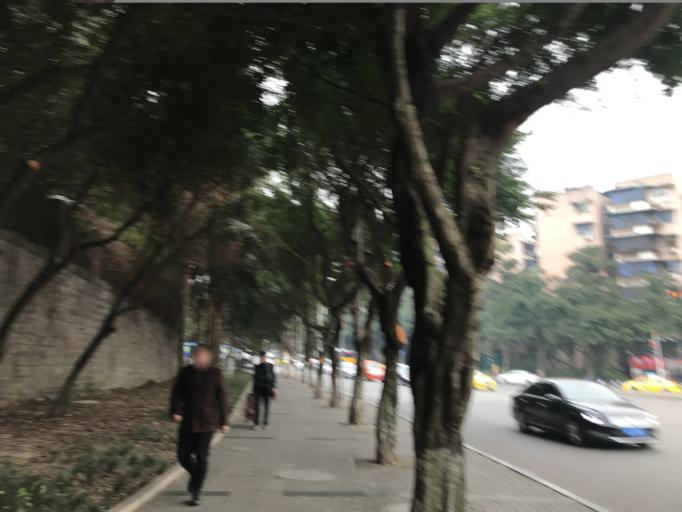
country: CN
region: Chongqing Shi
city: Chongqing
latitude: 29.5280
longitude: 106.5507
